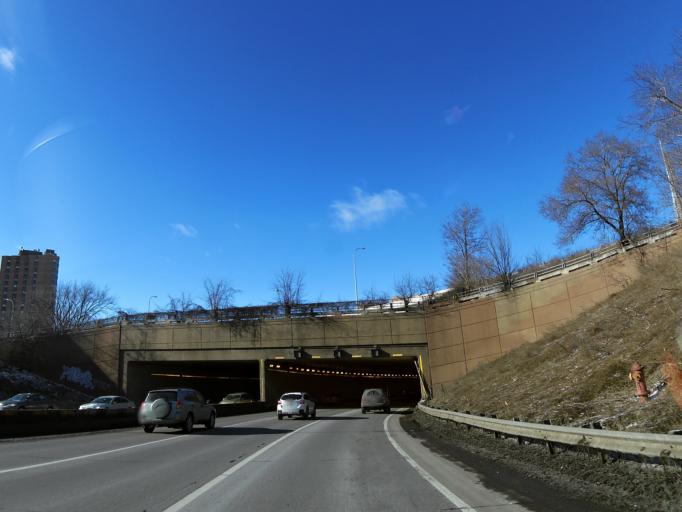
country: US
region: Minnesota
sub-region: Hennepin County
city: Minneapolis
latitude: 44.9649
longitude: -93.2869
